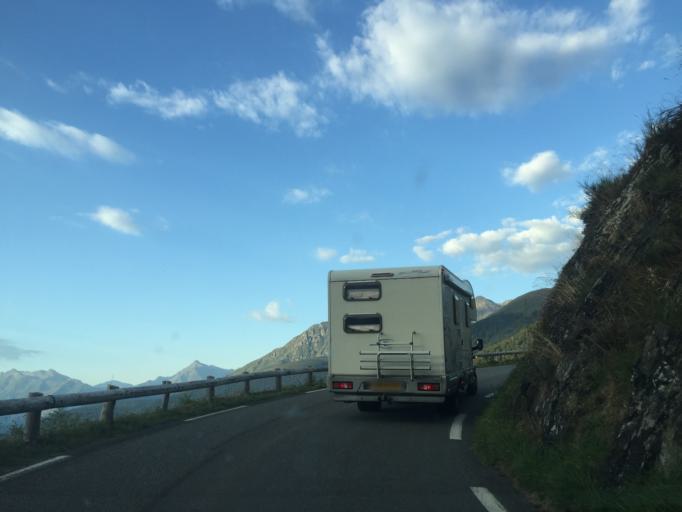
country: FR
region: Midi-Pyrenees
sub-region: Departement des Hautes-Pyrenees
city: Saint-Lary-Soulan
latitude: 42.9382
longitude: 0.3410
